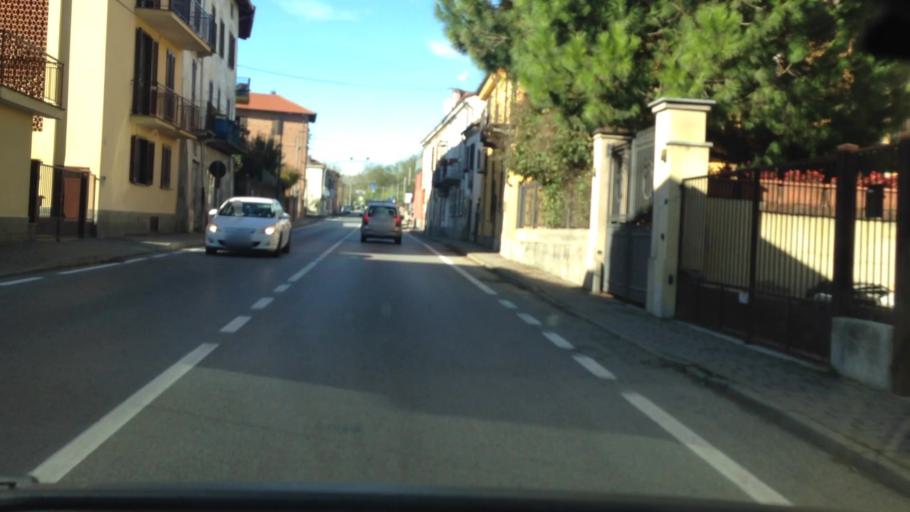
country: IT
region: Piedmont
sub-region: Provincia di Asti
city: Castello di Annone
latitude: 44.8805
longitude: 8.3139
